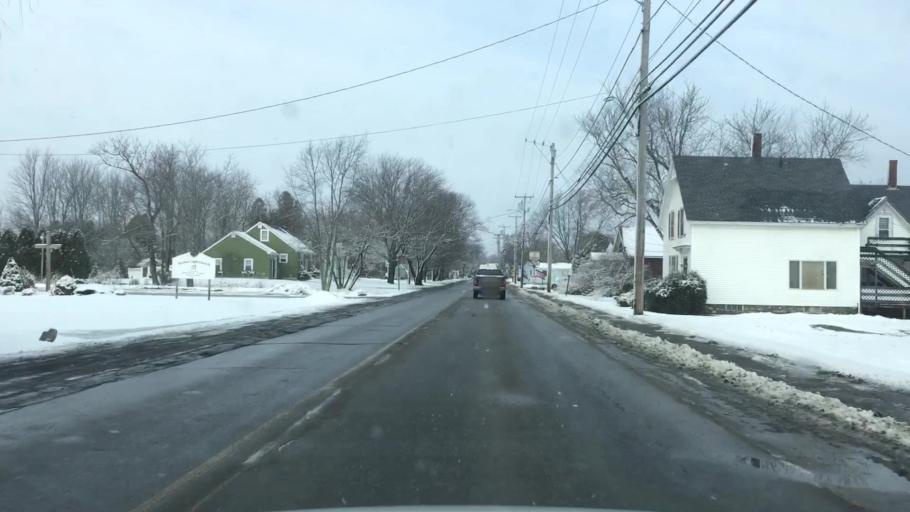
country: US
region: Maine
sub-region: Knox County
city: Rockland
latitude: 44.0931
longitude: -69.1106
